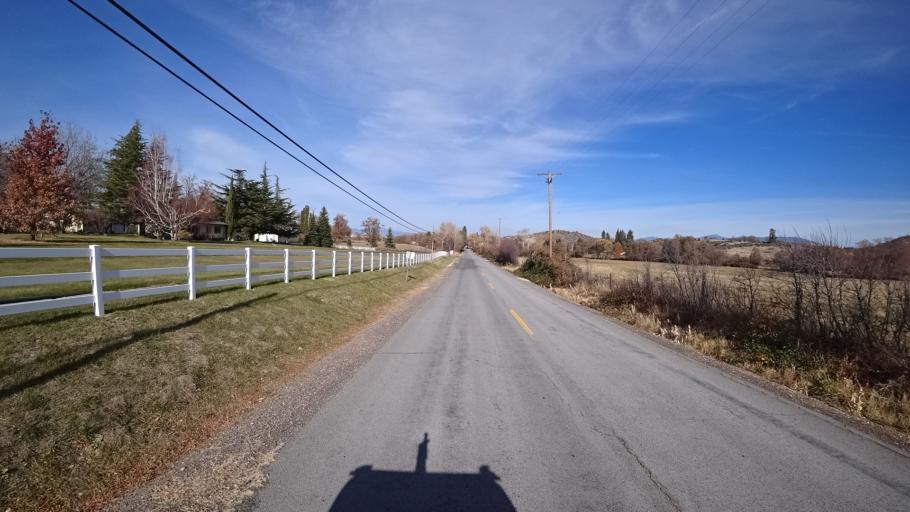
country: US
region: California
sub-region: Siskiyou County
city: Weed
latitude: 41.4527
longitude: -122.4311
